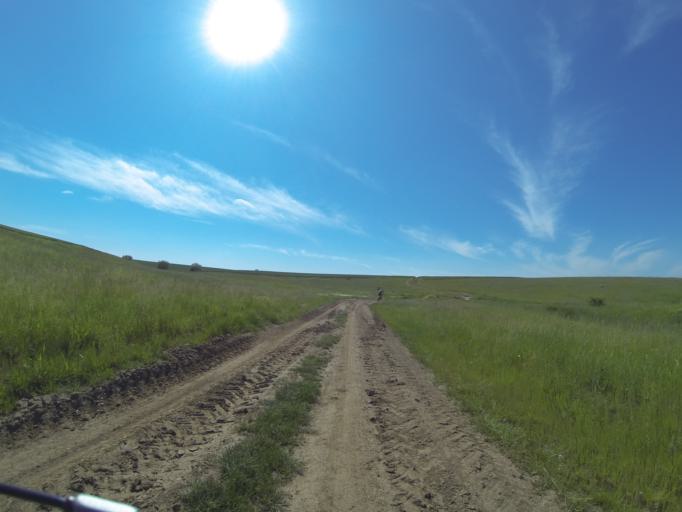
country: RO
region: Dolj
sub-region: Comuna Cosoveni
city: Cosoveni
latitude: 44.2608
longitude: 23.9767
